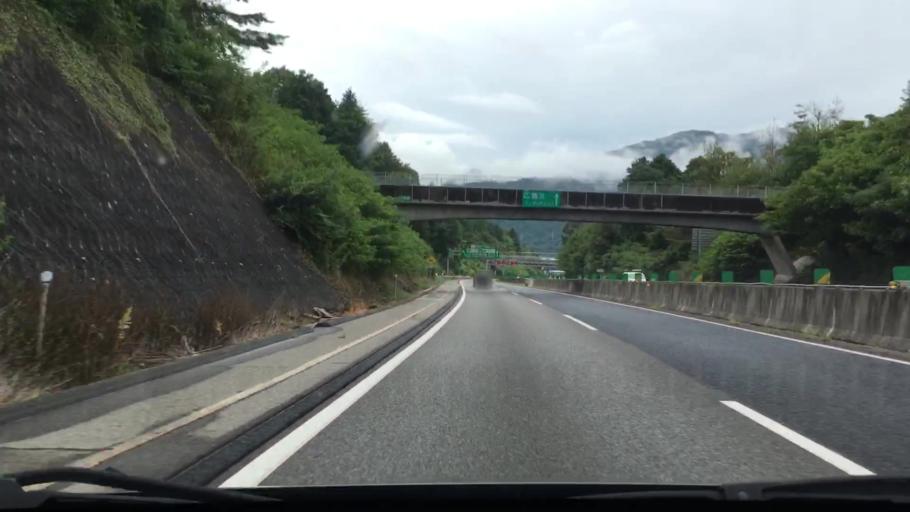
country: JP
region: Hiroshima
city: Hiroshima-shi
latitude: 34.5805
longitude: 132.4666
